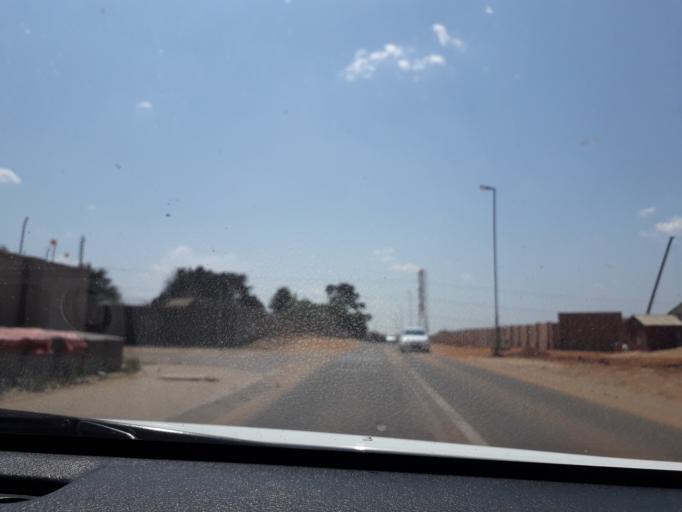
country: ZA
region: Gauteng
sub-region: City of Johannesburg Metropolitan Municipality
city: Modderfontein
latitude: -26.0780
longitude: 28.1985
